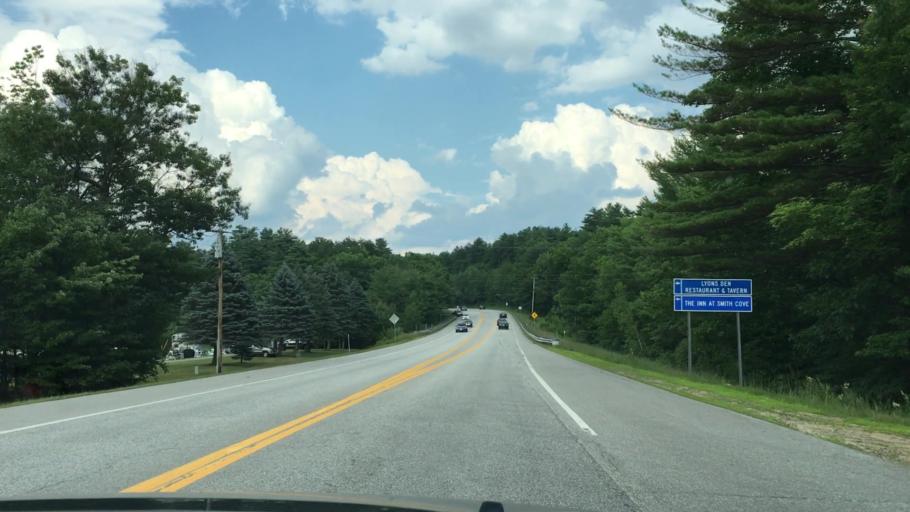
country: US
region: New Hampshire
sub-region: Belknap County
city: Gilford
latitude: 43.5797
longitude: -71.3943
